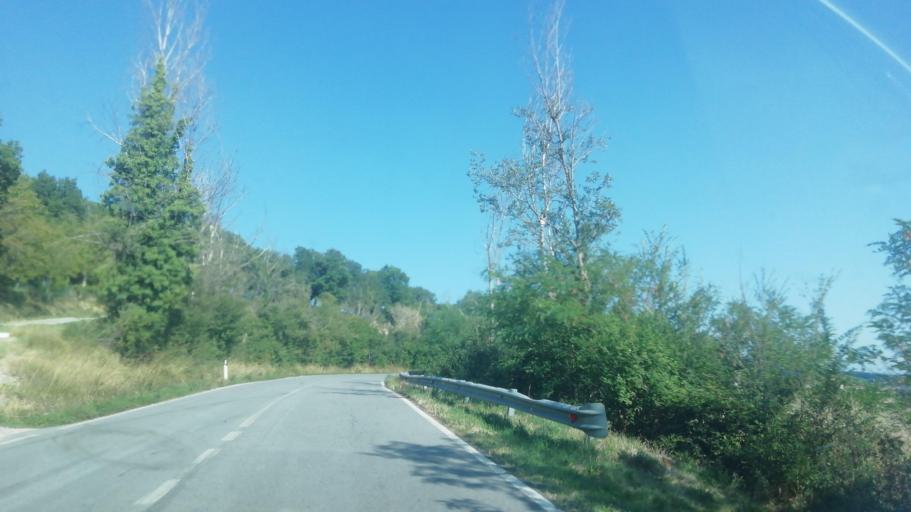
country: IT
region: The Marches
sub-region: Provincia di Pesaro e Urbino
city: Frontone
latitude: 43.5390
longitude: 12.7316
